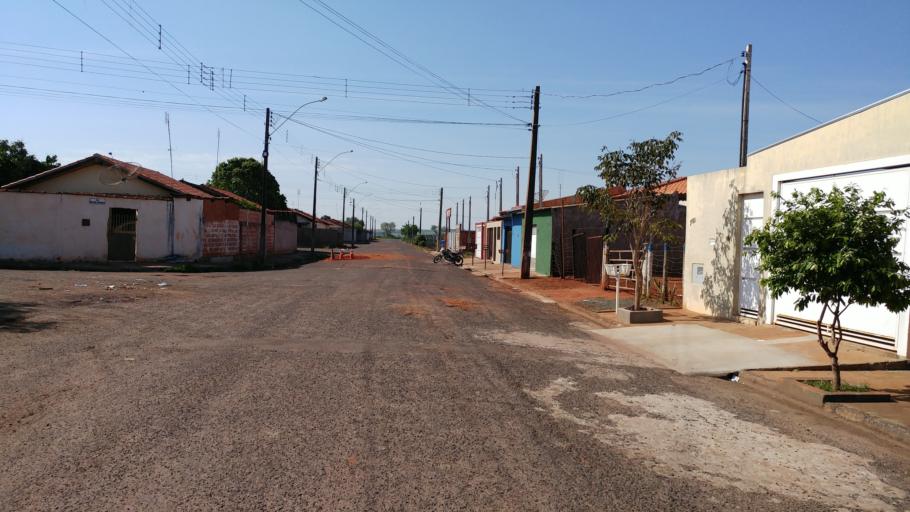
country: BR
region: Sao Paulo
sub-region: Paraguacu Paulista
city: Paraguacu Paulista
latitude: -22.4088
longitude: -50.5632
